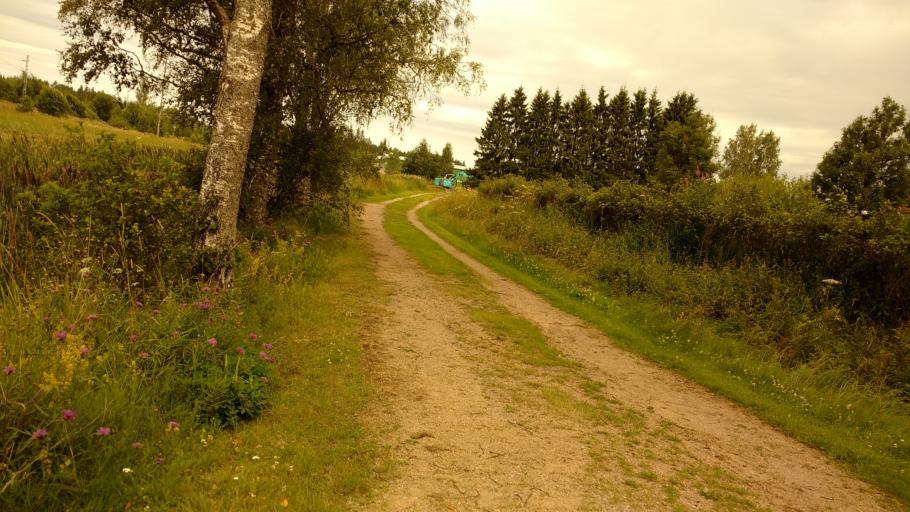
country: FI
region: Varsinais-Suomi
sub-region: Turku
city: Piikkioe
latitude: 60.4315
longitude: 22.4682
